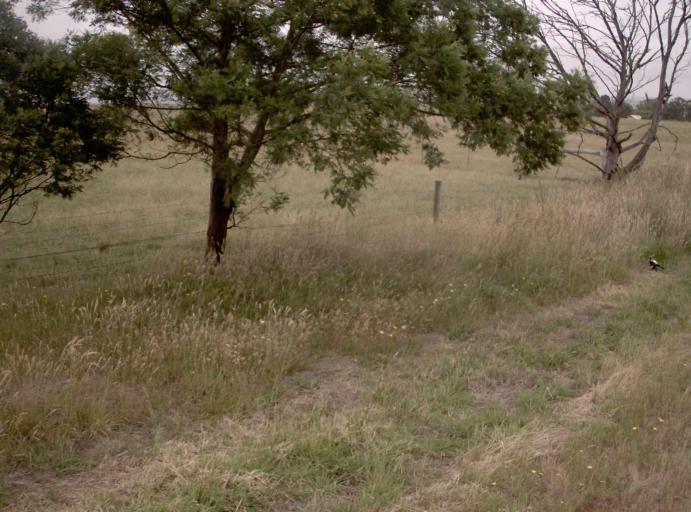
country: AU
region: Victoria
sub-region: East Gippsland
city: Bairnsdale
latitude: -37.8113
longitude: 147.4374
